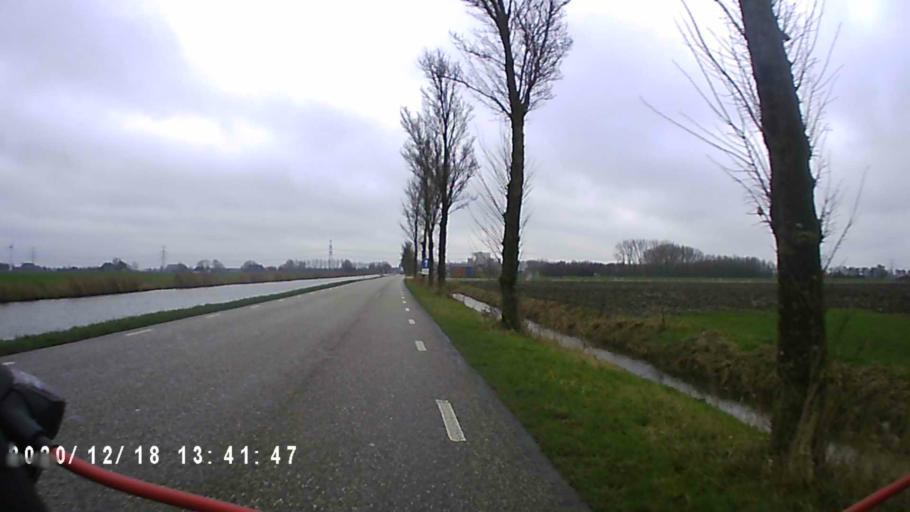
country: NL
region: Groningen
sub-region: Gemeente Bedum
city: Bedum
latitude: 53.3197
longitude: 6.5965
